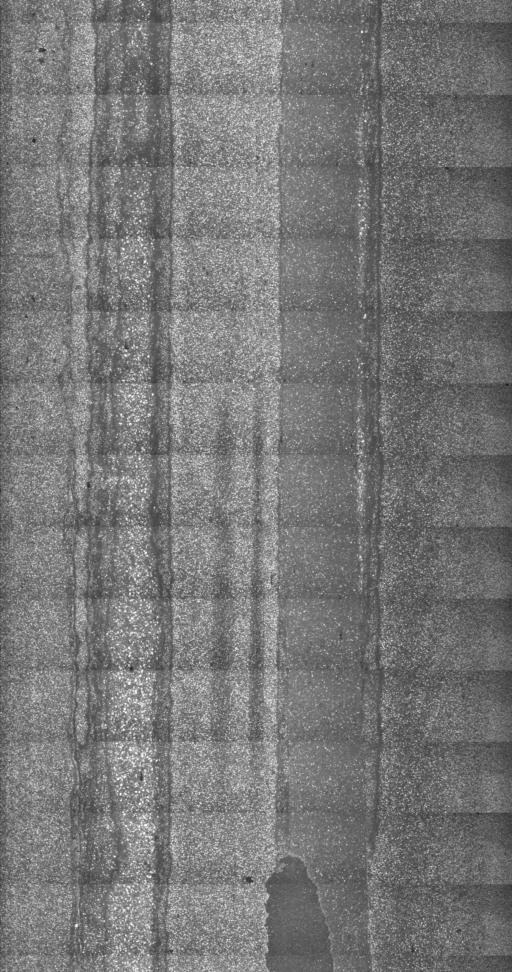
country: US
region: Vermont
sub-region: Washington County
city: Barre
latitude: 44.1945
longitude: -72.5010
